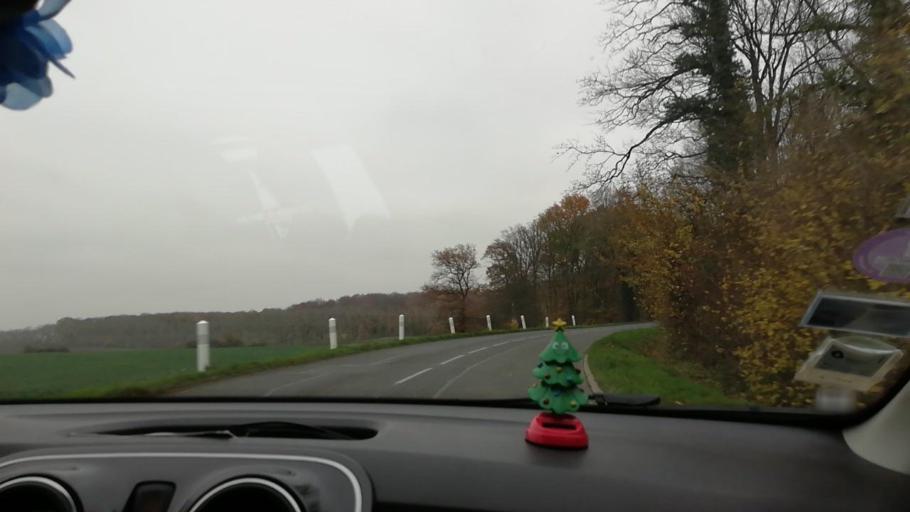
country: FR
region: Ile-de-France
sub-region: Departement de Seine-et-Marne
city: Juilly
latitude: 49.0392
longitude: 2.7418
